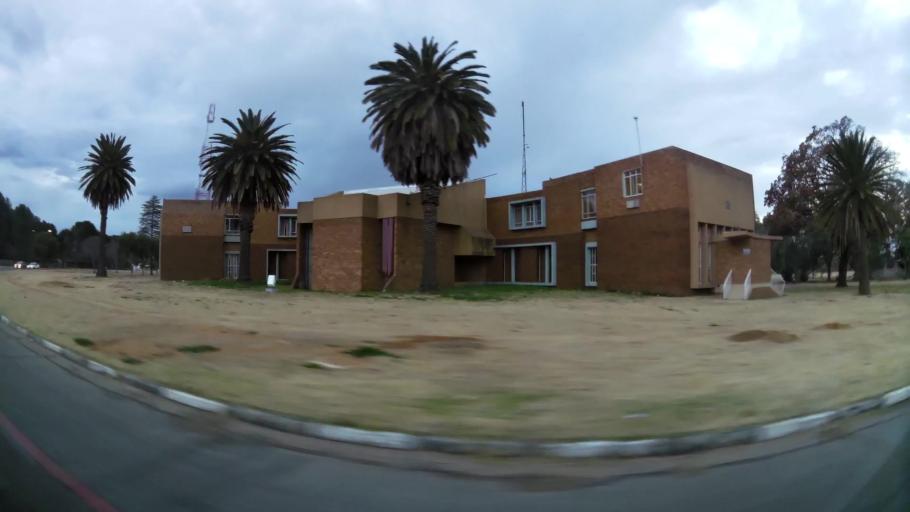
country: ZA
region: Orange Free State
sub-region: Lejweleputswa District Municipality
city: Welkom
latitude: -27.9774
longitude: 26.7450
